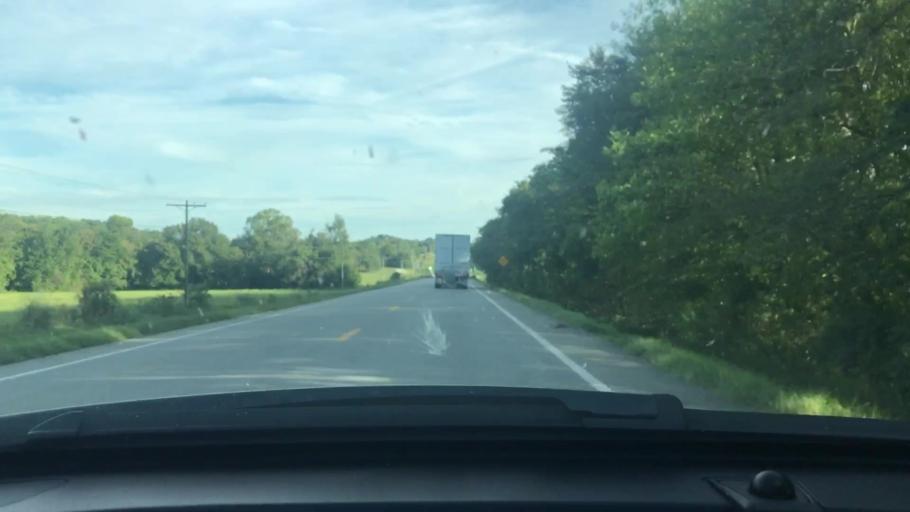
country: US
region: Arkansas
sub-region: Randolph County
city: Pocahontas
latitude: 36.1951
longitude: -91.1672
